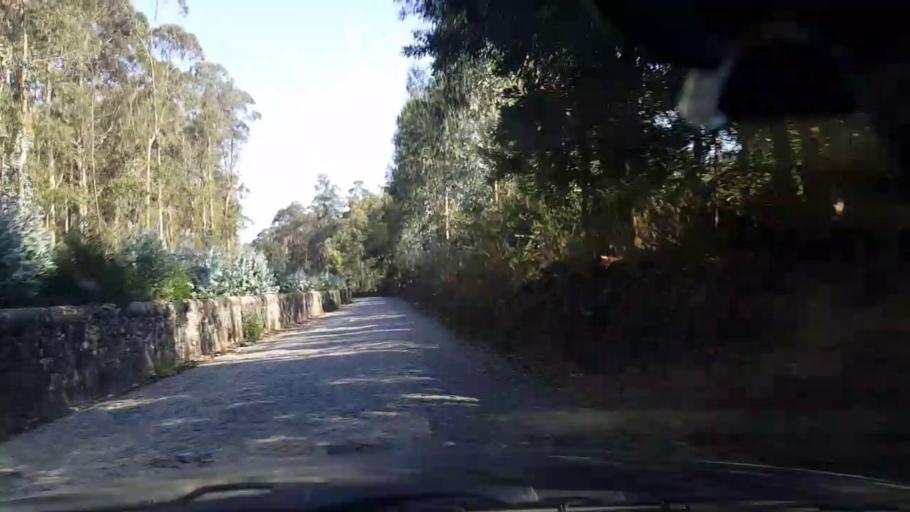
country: PT
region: Porto
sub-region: Vila do Conde
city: Arvore
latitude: 41.3519
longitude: -8.7027
